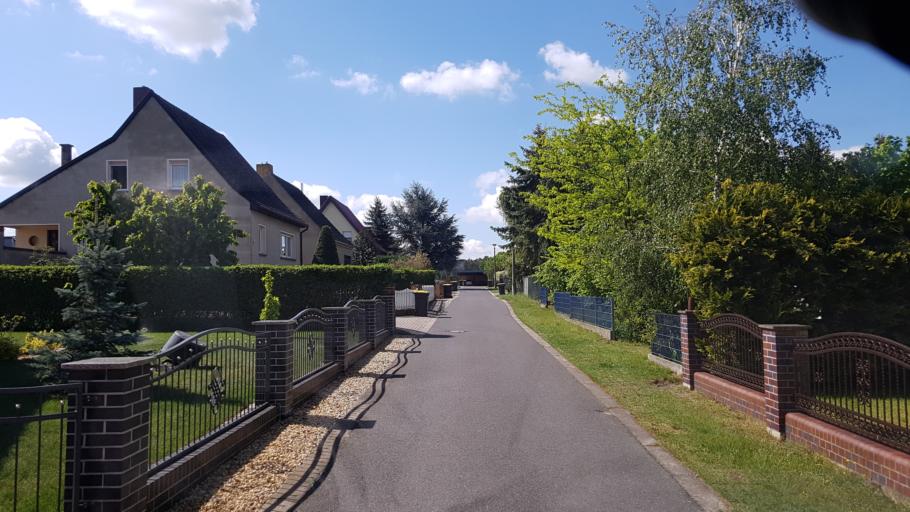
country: DE
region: Brandenburg
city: Bronkow
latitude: 51.5915
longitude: 13.9249
